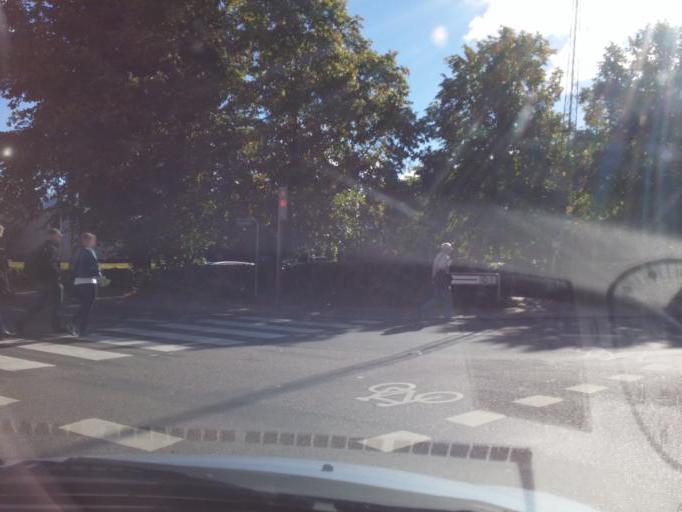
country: DK
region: South Denmark
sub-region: Odense Kommune
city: Odense
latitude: 55.3923
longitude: 10.3794
